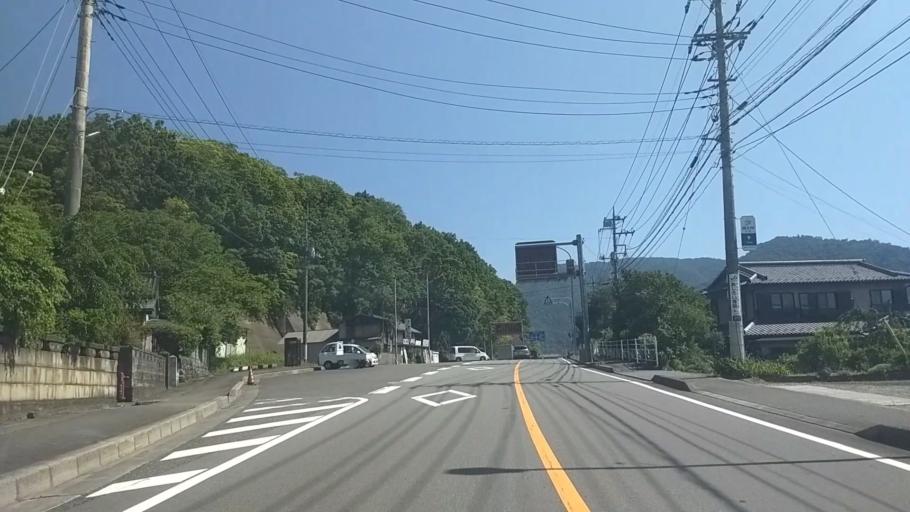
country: JP
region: Yamanashi
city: Ryuo
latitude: 35.4159
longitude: 138.4430
